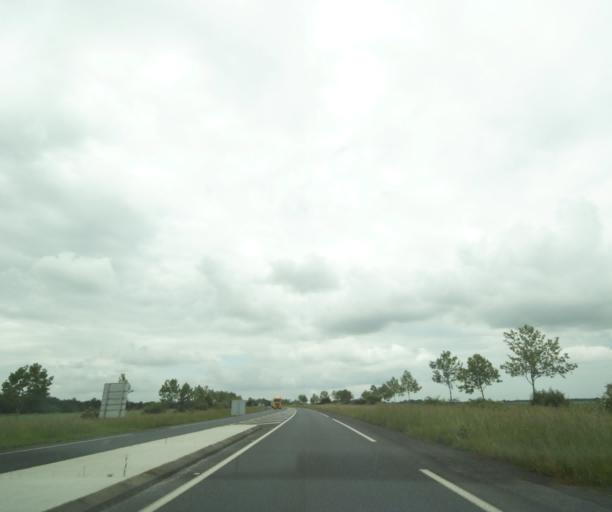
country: FR
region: Poitou-Charentes
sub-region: Departement des Deux-Sevres
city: Saint-Varent
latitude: 46.9028
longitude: -0.1908
